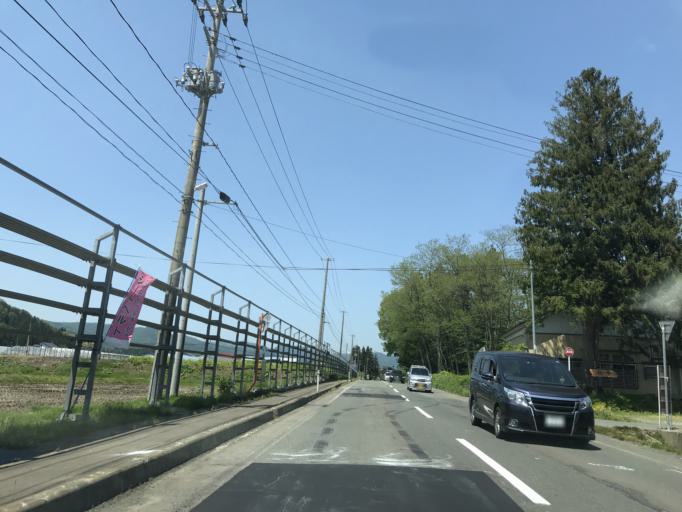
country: JP
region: Akita
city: Yokotemachi
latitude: 39.3876
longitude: 140.7581
